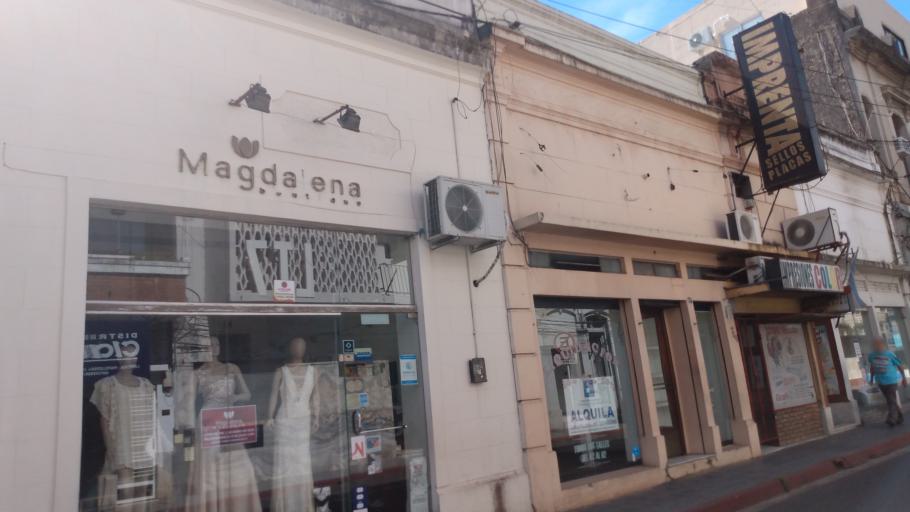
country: AR
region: Corrientes
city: Corrientes
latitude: -27.4658
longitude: -58.8379
